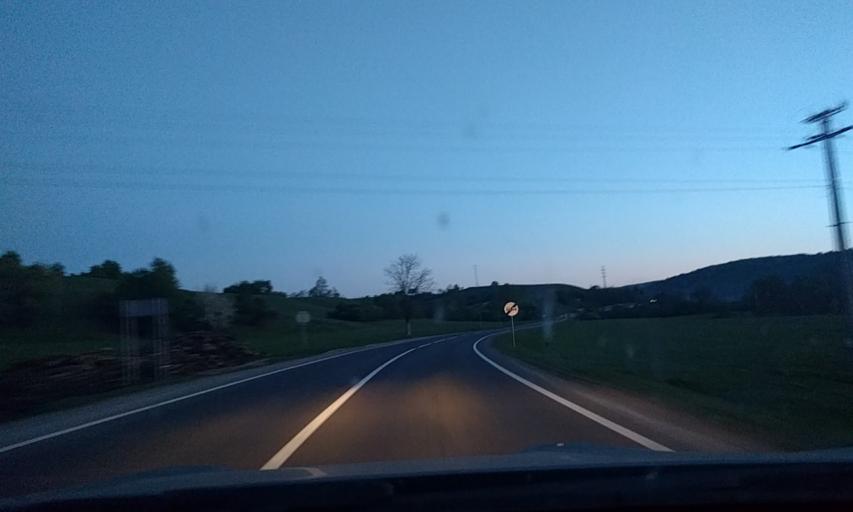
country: RO
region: Mures
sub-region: Comuna Saschiz
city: Saschiz
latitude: 46.2267
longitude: 24.9793
